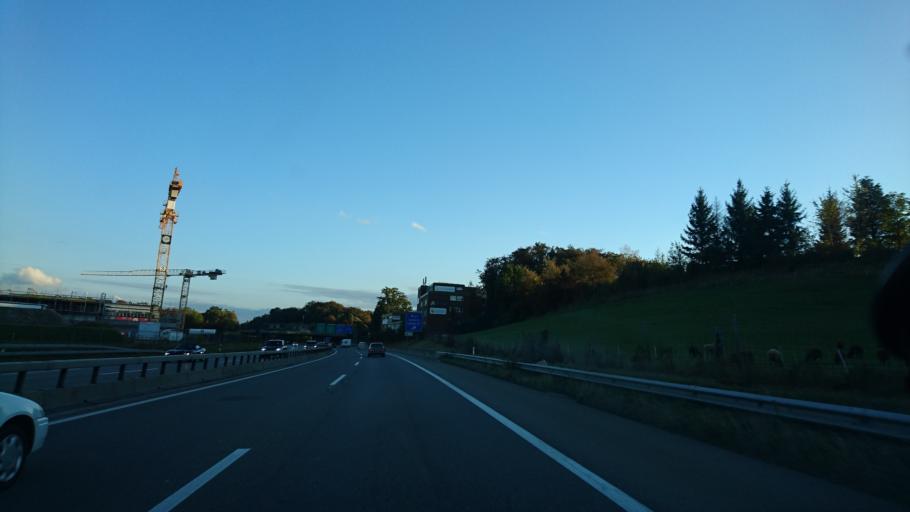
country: CH
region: Bern
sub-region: Bern-Mittelland District
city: Muri
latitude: 46.9282
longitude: 7.5009
